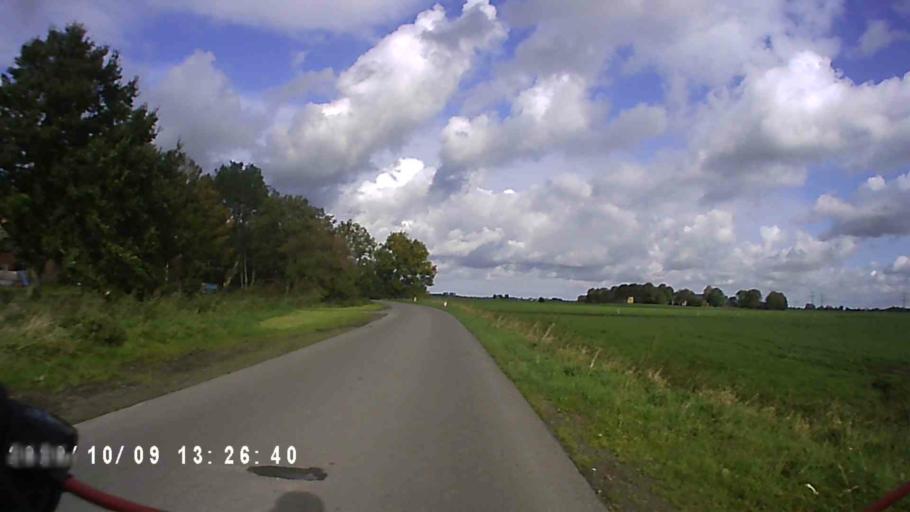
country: NL
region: Groningen
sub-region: Gemeente Zuidhorn
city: Aduard
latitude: 53.2652
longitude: 6.4634
